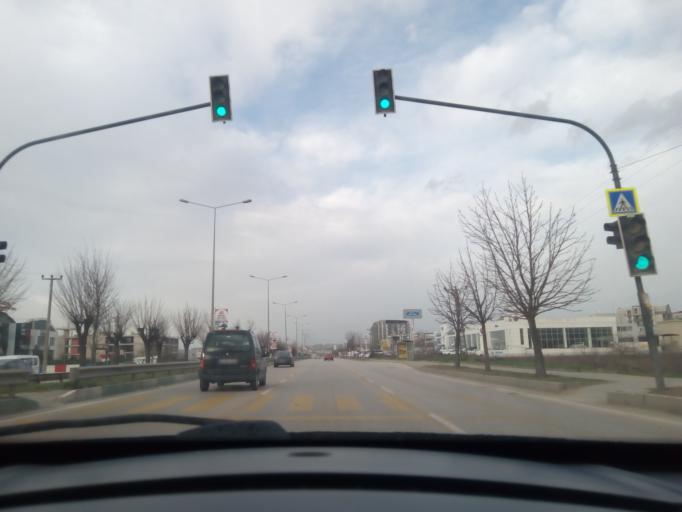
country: TR
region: Bursa
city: Cali
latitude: 40.2142
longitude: 28.9099
